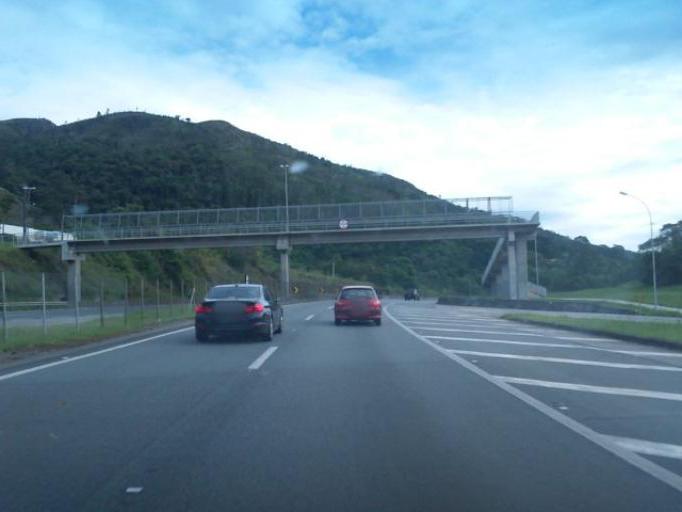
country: BR
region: Parana
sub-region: Campina Grande Do Sul
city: Campina Grande do Sul
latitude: -25.1395
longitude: -48.8563
